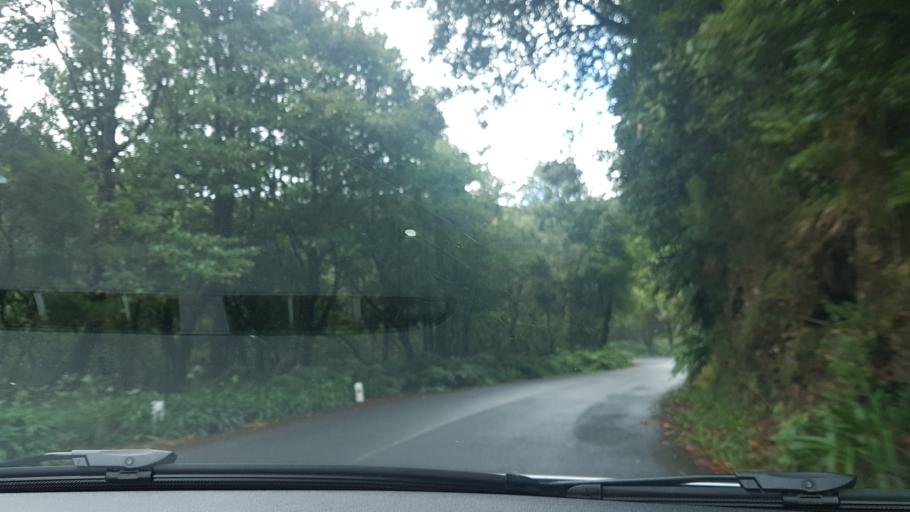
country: PT
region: Madeira
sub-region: Sao Vicente
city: Sao Vicente
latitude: 32.7570
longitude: -17.0171
